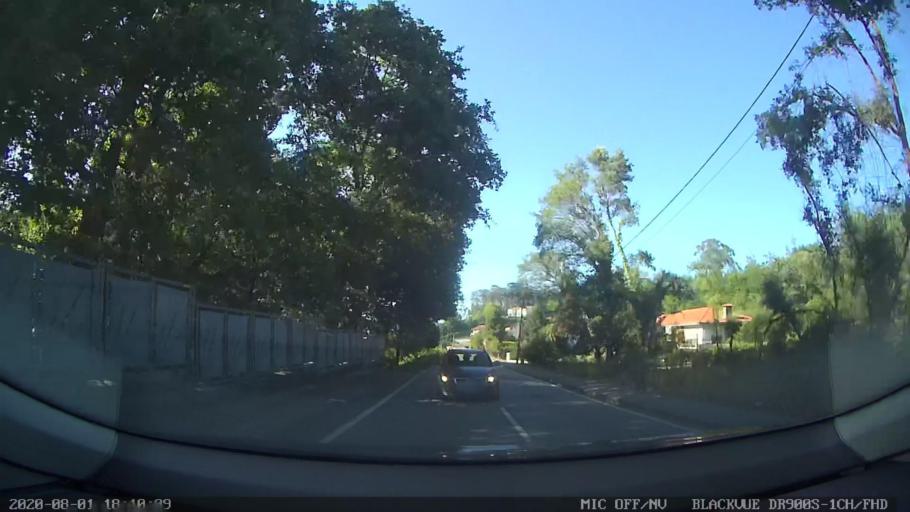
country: PT
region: Porto
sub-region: Santo Tirso
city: Sao Miguel do Couto
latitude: 41.3066
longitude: -8.4709
